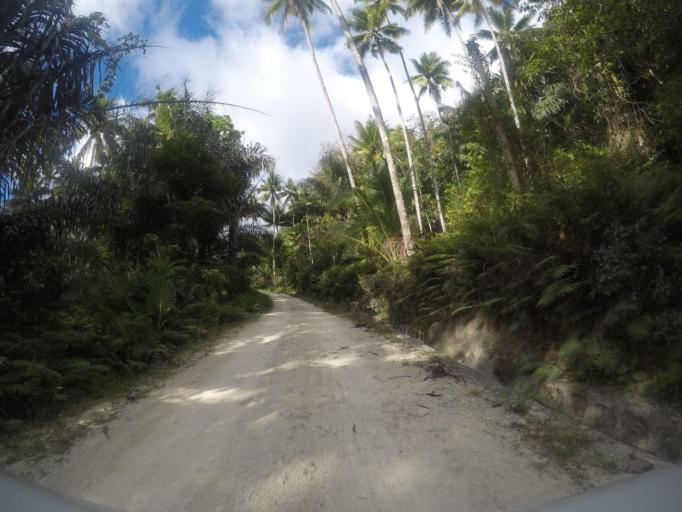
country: TL
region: Lautem
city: Lospalos
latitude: -8.5258
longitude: 126.9372
